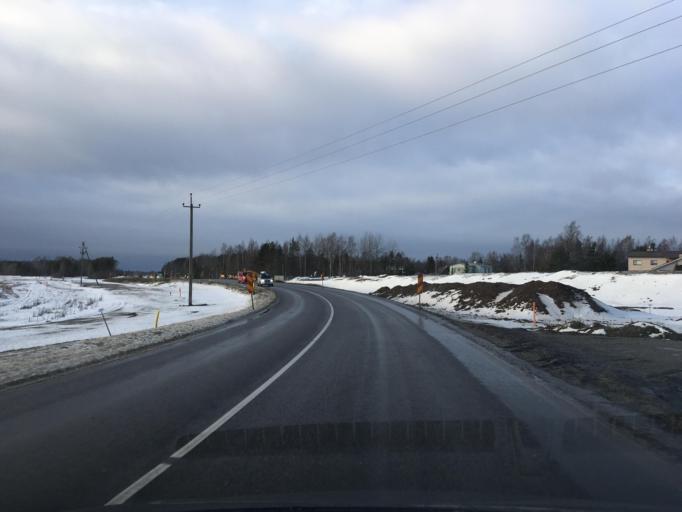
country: EE
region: Harju
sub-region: Saue linn
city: Saue
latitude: 59.3105
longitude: 24.5570
